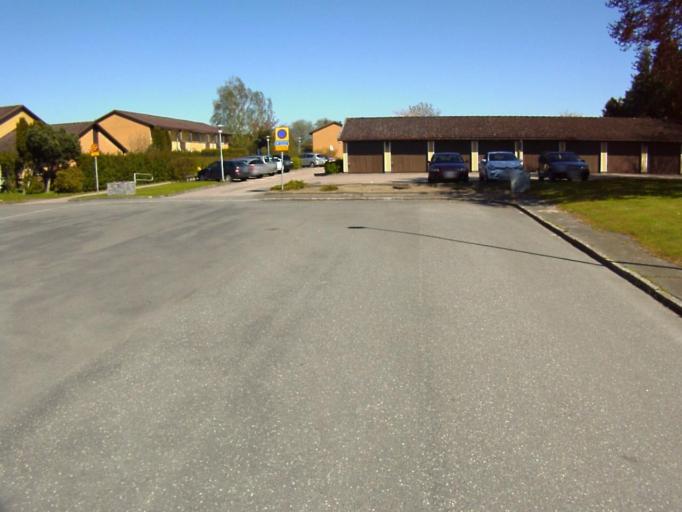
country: SE
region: Skane
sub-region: Kristianstads Kommun
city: Kristianstad
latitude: 56.0291
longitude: 14.2028
